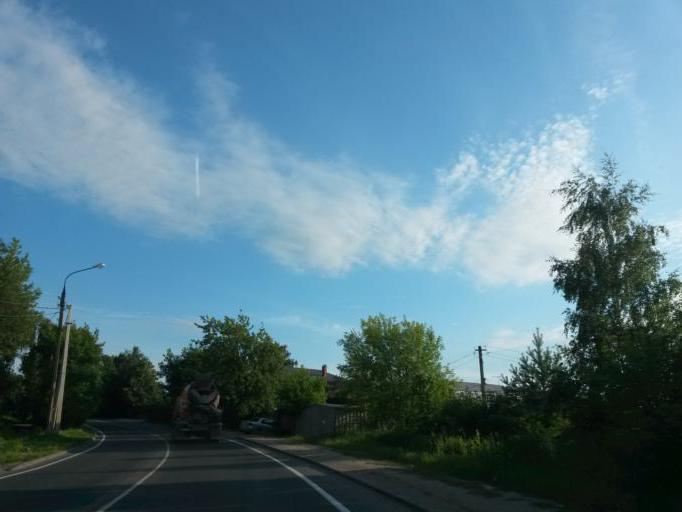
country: RU
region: Moskovskaya
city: Yam
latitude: 55.4662
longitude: 37.7020
